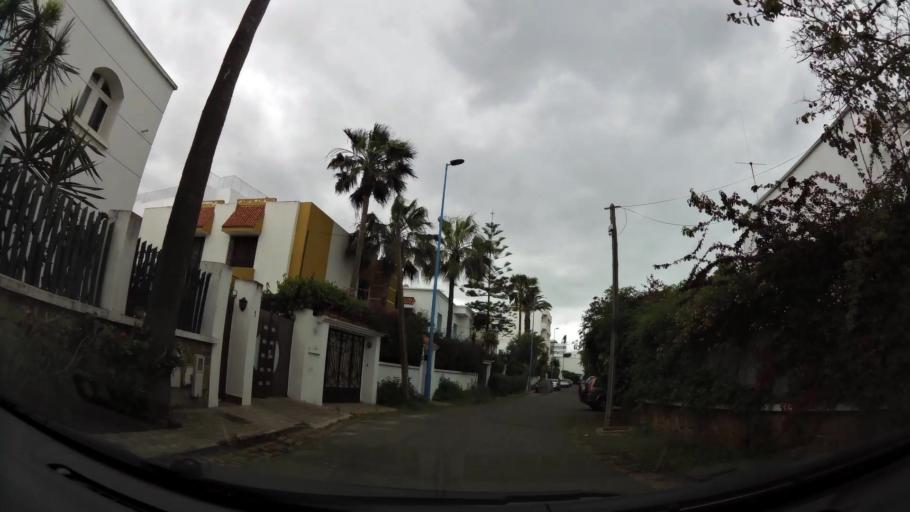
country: MA
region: Grand Casablanca
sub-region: Casablanca
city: Casablanca
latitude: 33.5664
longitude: -7.6426
